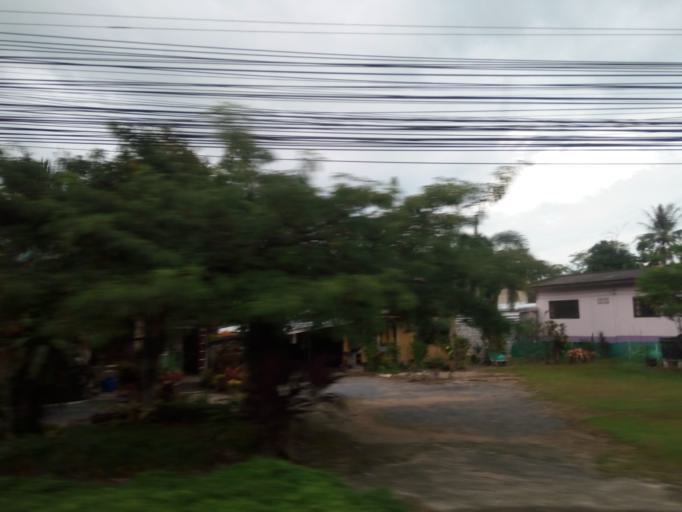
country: TH
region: Phuket
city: Thalang
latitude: 8.0782
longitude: 98.3833
